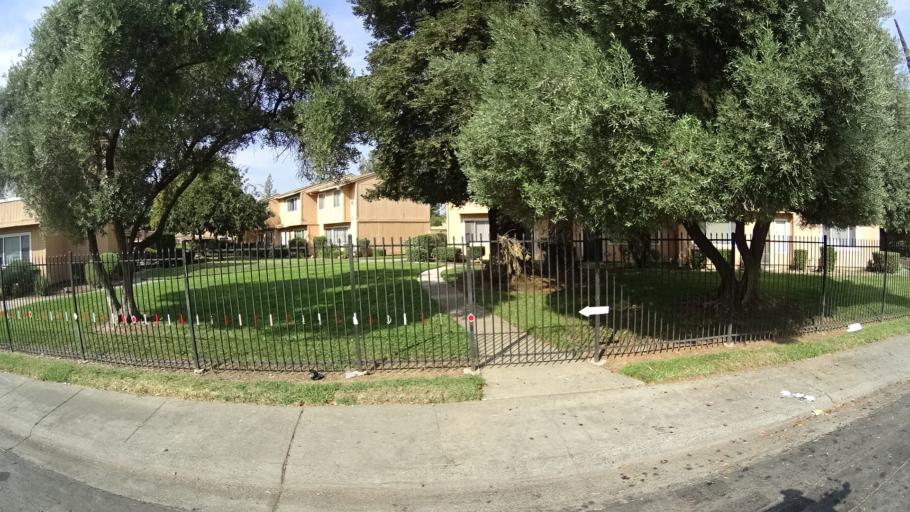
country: US
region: California
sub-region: Sacramento County
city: Florin
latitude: 38.4714
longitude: -121.4313
